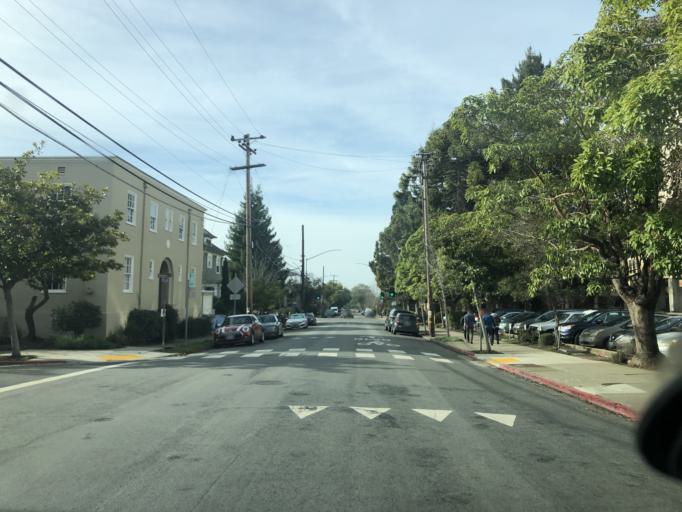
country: US
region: California
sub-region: Alameda County
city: Berkeley
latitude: 37.8578
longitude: -122.2584
